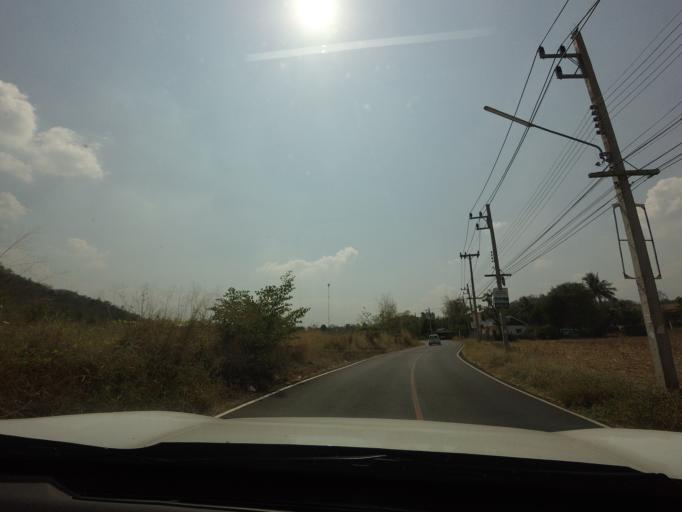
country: TH
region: Nakhon Ratchasima
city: Pak Chong
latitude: 14.5802
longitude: 101.4366
